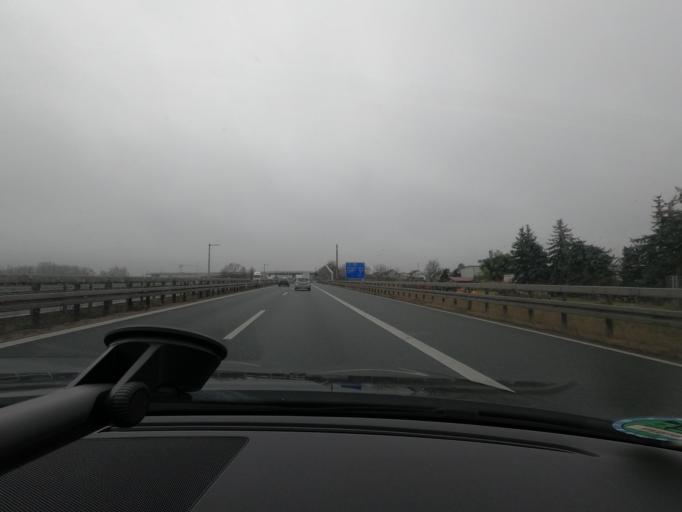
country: DE
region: Bavaria
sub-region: Regierungsbezirk Mittelfranken
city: Baiersdorf
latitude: 49.6702
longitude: 11.0455
